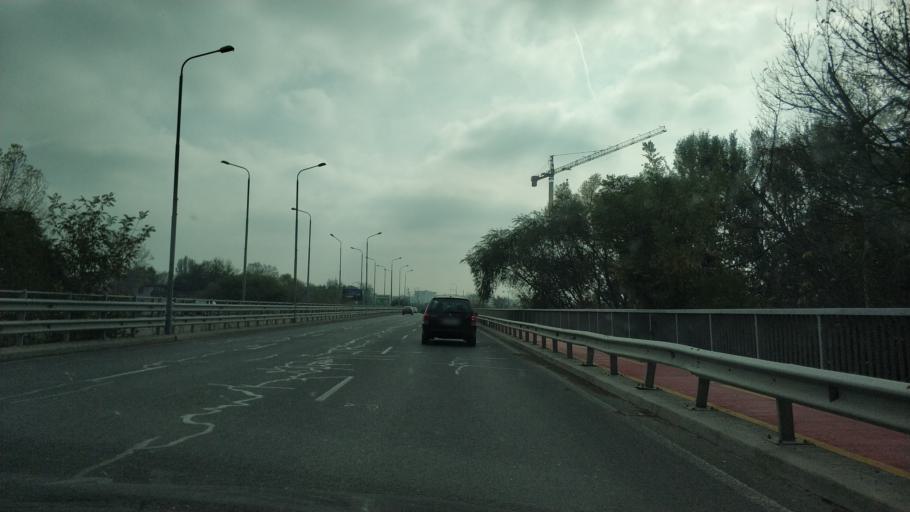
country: BG
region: Plovdiv
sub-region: Obshtina Plovdiv
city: Plovdiv
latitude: 42.1555
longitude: 24.7655
